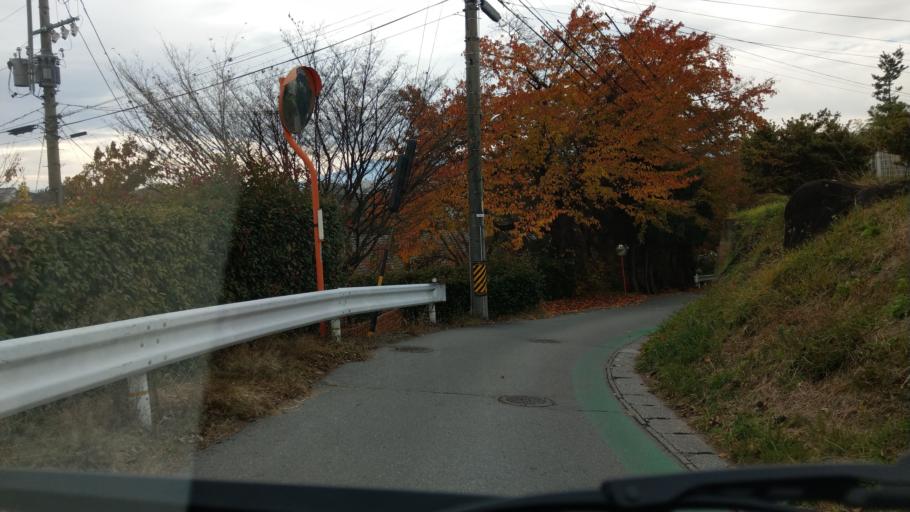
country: JP
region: Nagano
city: Komoro
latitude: 36.3152
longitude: 138.4593
